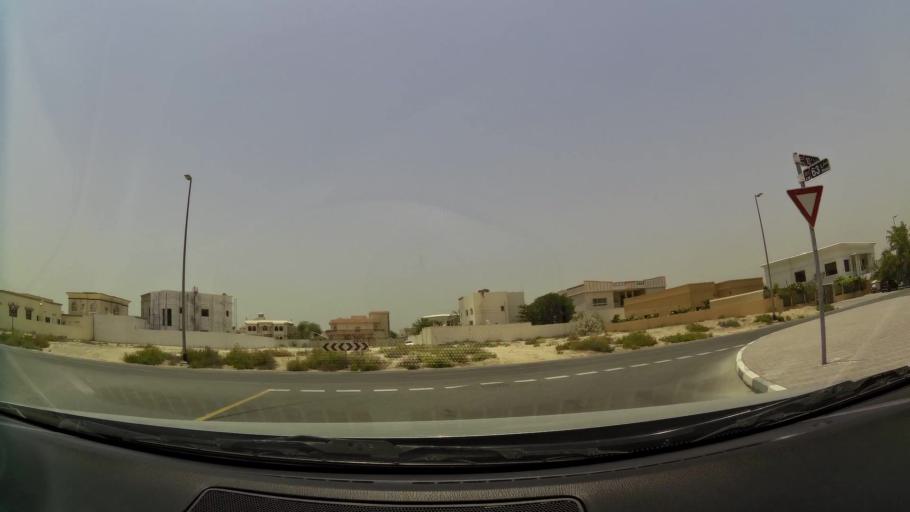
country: AE
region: Ash Shariqah
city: Sharjah
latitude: 25.2091
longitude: 55.3815
